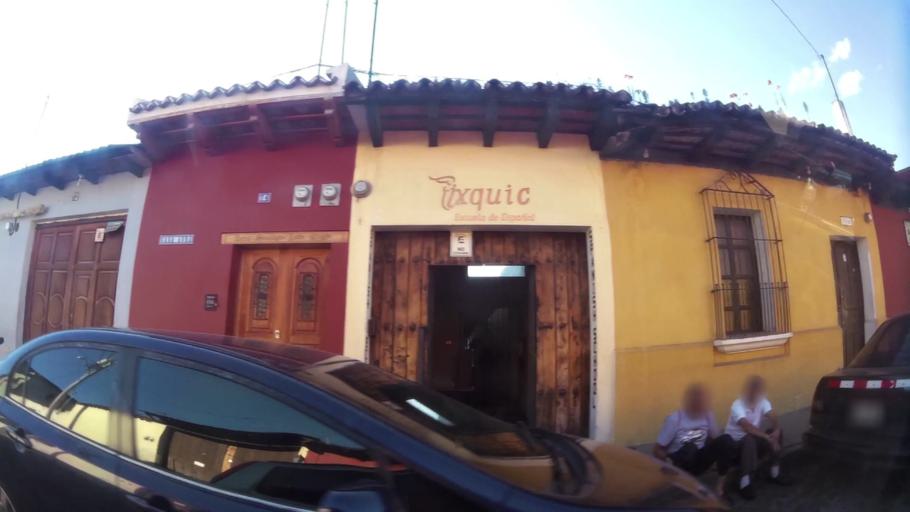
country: GT
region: Sacatepequez
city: Antigua Guatemala
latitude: 14.5611
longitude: -90.7363
